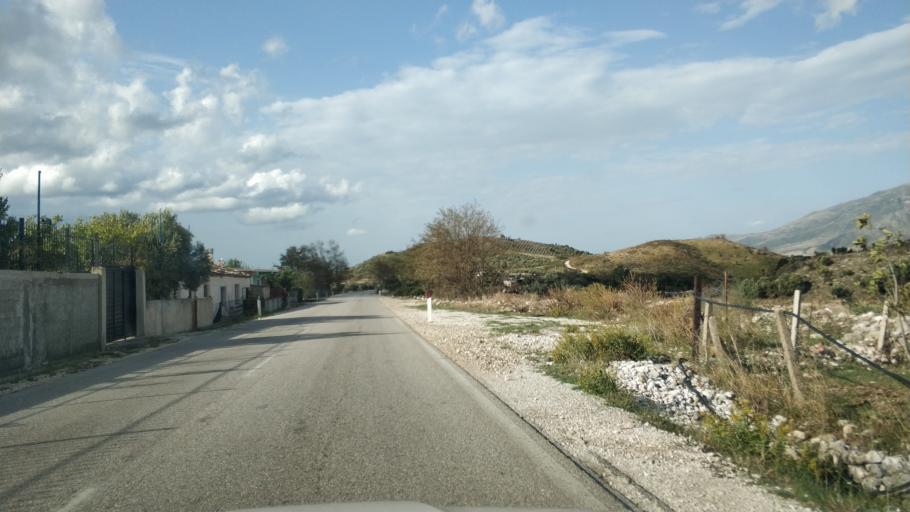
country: AL
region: Vlore
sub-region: Rrethi i Vlores
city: Orikum
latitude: 40.2918
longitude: 19.4917
